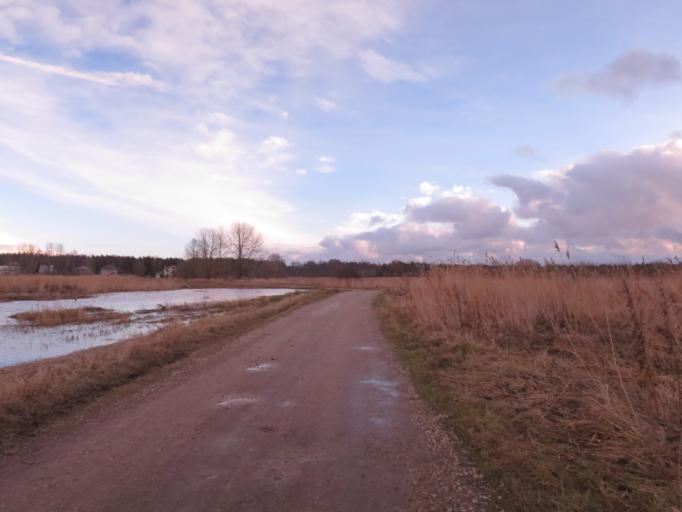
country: LV
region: Riga
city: Bolderaja
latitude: 57.0555
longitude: 24.0950
